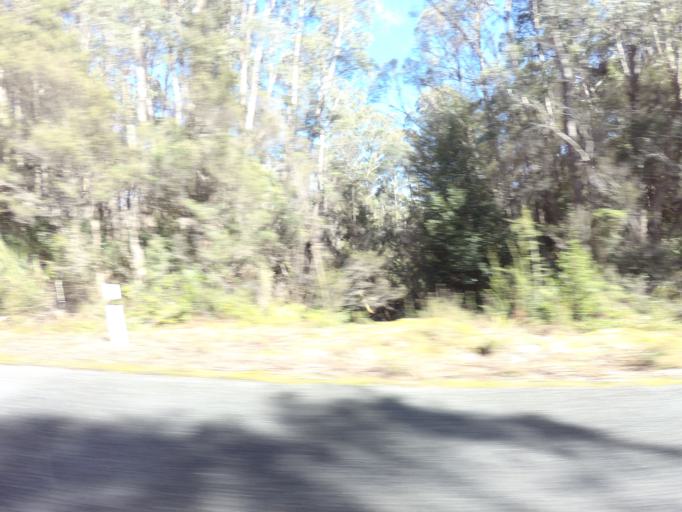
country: AU
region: Tasmania
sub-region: Derwent Valley
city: New Norfolk
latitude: -42.7518
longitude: 146.4114
